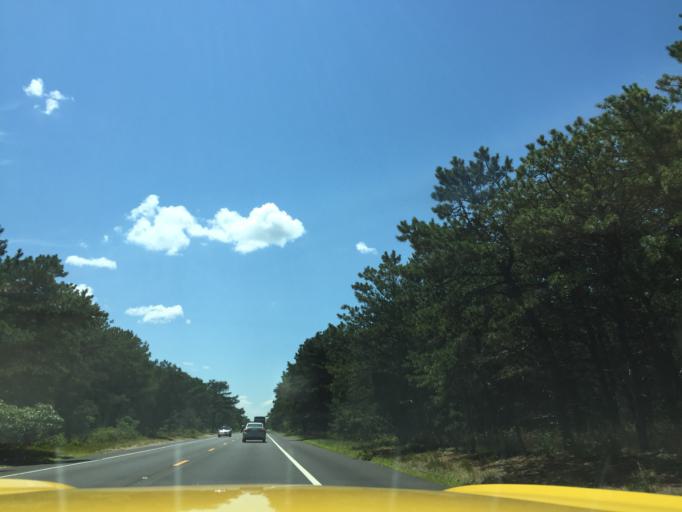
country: US
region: New York
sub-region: Suffolk County
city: Amagansett
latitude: 40.9898
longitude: -72.0758
